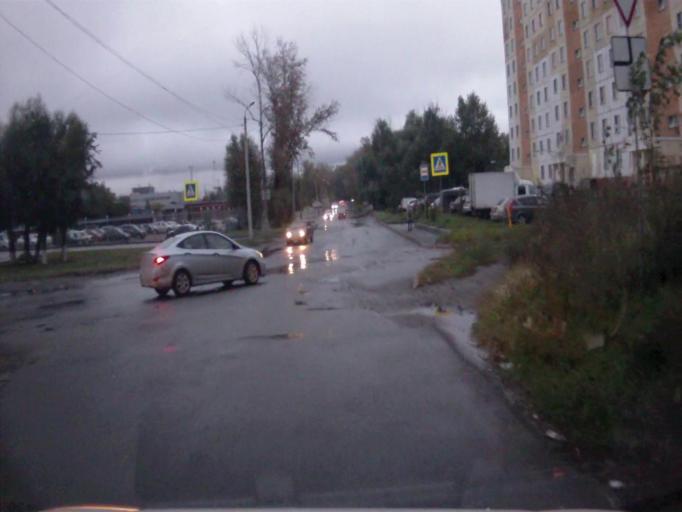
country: RU
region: Chelyabinsk
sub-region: Gorod Chelyabinsk
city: Chelyabinsk
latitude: 55.1391
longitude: 61.4535
